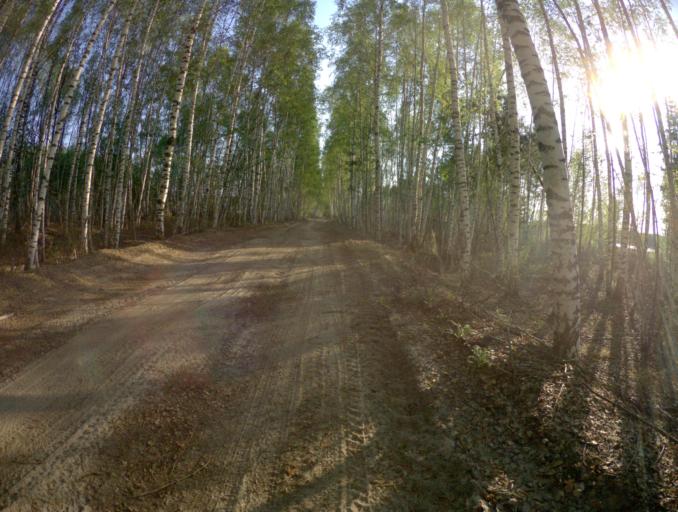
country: RU
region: Vladimir
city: Vyazniki
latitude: 56.3697
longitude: 42.1604
